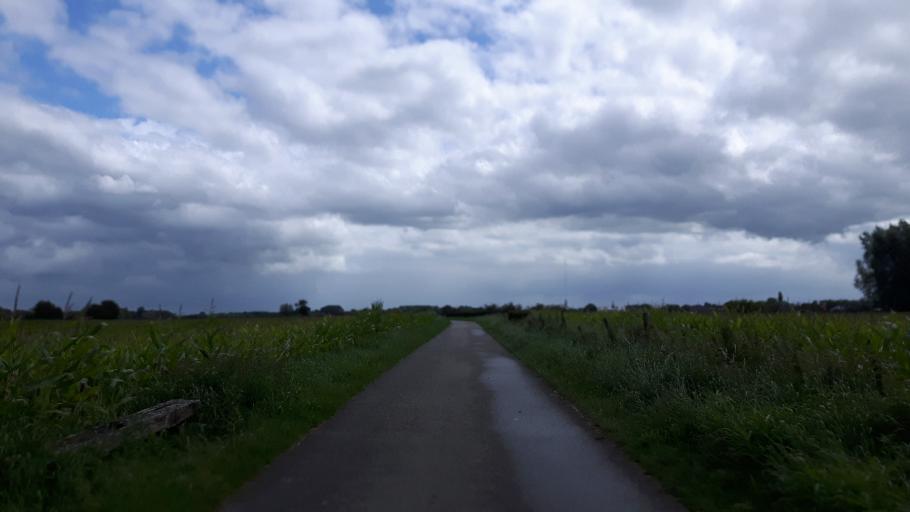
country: NL
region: Utrecht
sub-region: Gemeente IJsselstein
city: IJsselstein
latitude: 52.0444
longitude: 5.0155
